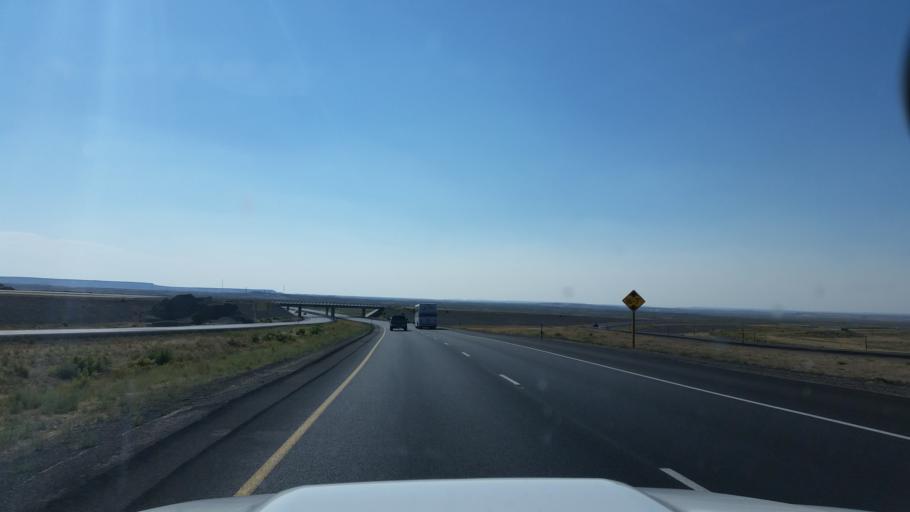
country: US
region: Wyoming
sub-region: Sweetwater County
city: Green River
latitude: 41.5444
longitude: -109.9056
